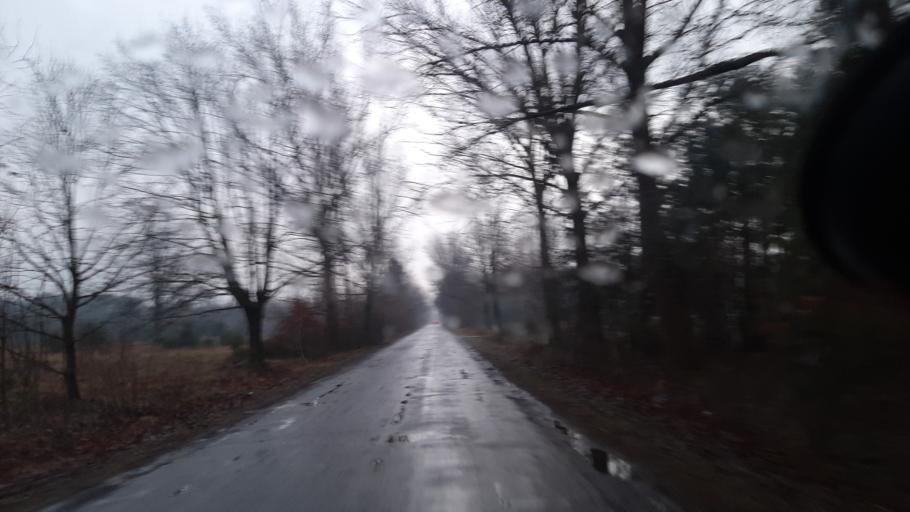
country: PL
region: Lublin Voivodeship
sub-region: Powiat lubartowski
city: Firlej
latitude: 51.5241
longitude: 22.4997
